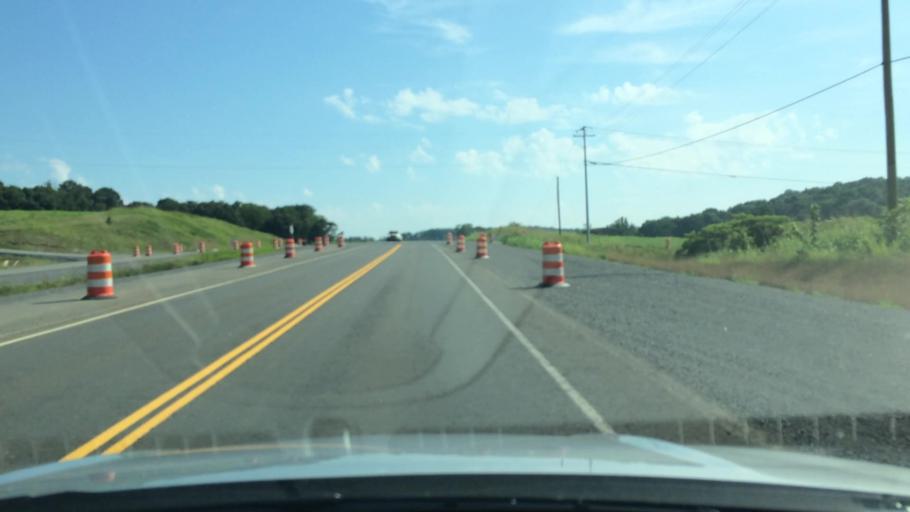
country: US
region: Tennessee
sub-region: Jefferson County
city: White Pine
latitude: 36.1160
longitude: -83.3405
